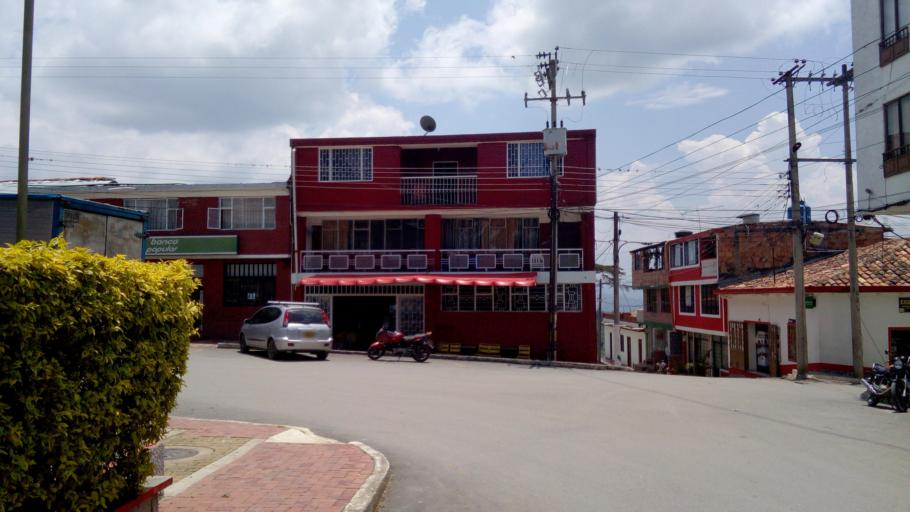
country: CO
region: Boyaca
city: Santana
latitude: 6.0576
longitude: -73.4827
